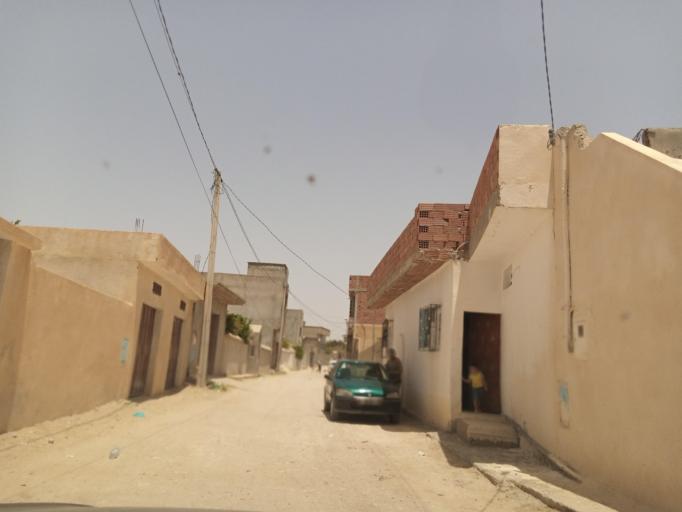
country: TN
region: Al Qasrayn
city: Kasserine
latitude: 35.2131
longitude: 8.8922
